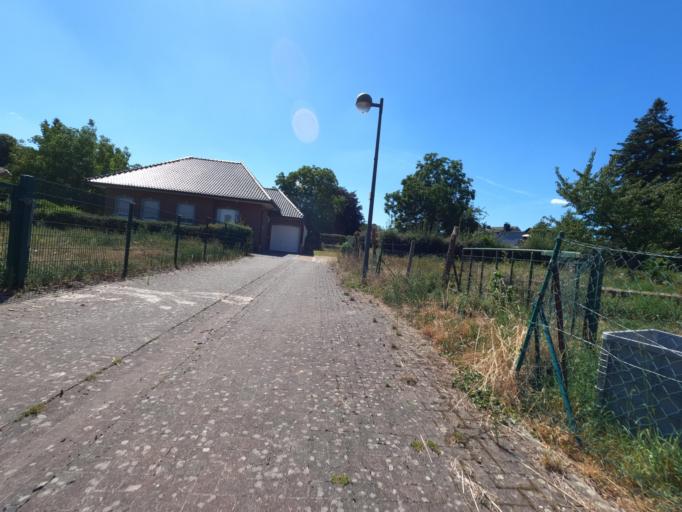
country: DE
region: North Rhine-Westphalia
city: Baesweiler
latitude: 50.9057
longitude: 6.1817
